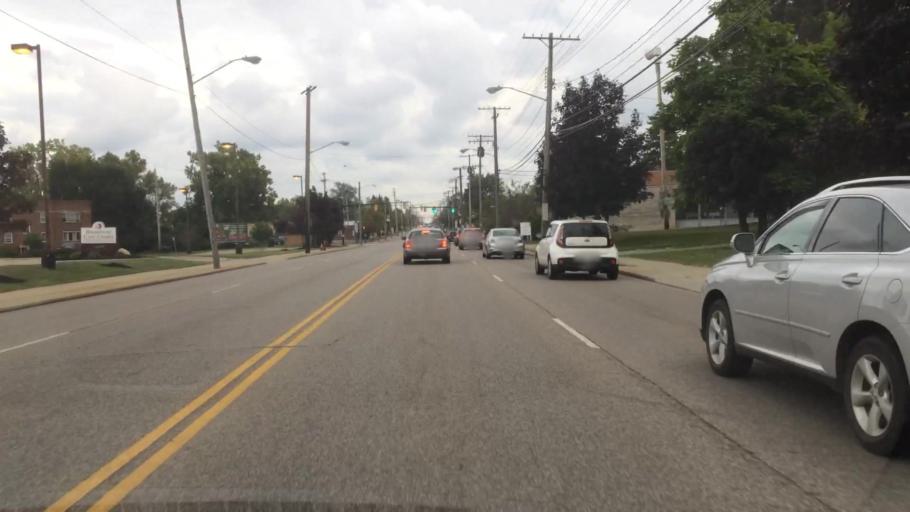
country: US
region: Ohio
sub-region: Cuyahoga County
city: Maple Heights
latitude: 41.4148
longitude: -81.5691
